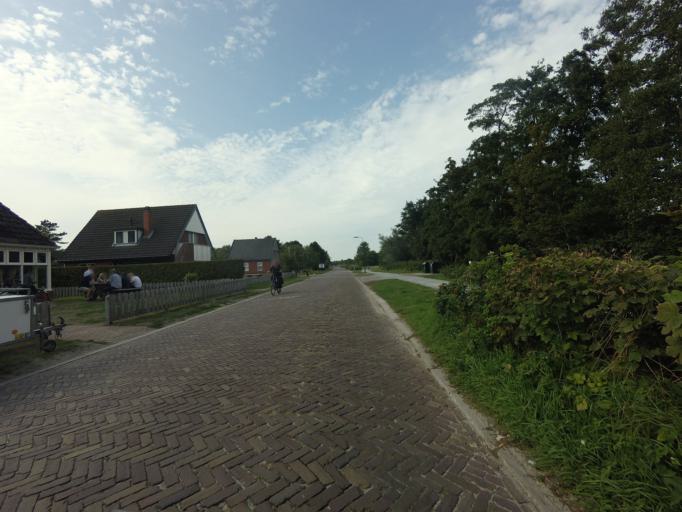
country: NL
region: Friesland
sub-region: Gemeente Schiermonnikoog
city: Schiermonnikoog
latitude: 53.4825
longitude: 6.1597
